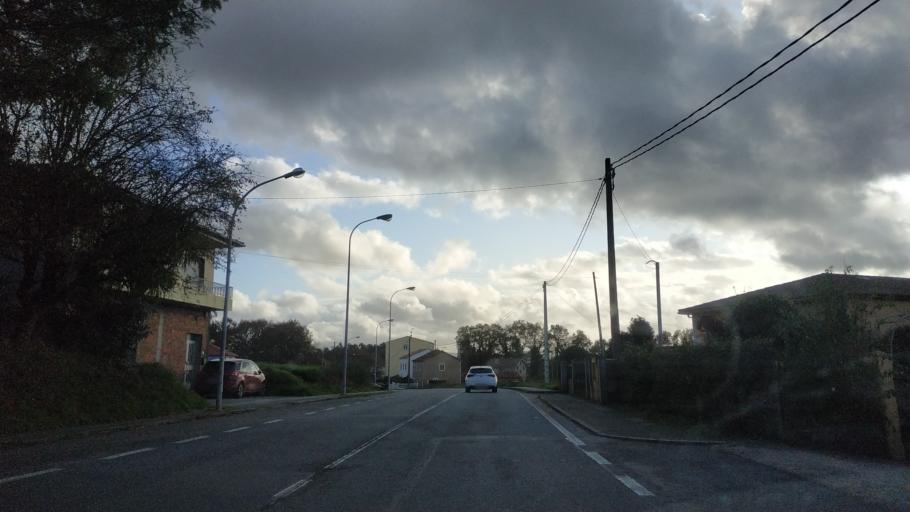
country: ES
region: Galicia
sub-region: Provincia da Coruna
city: Arzua
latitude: 42.9210
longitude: -8.1654
